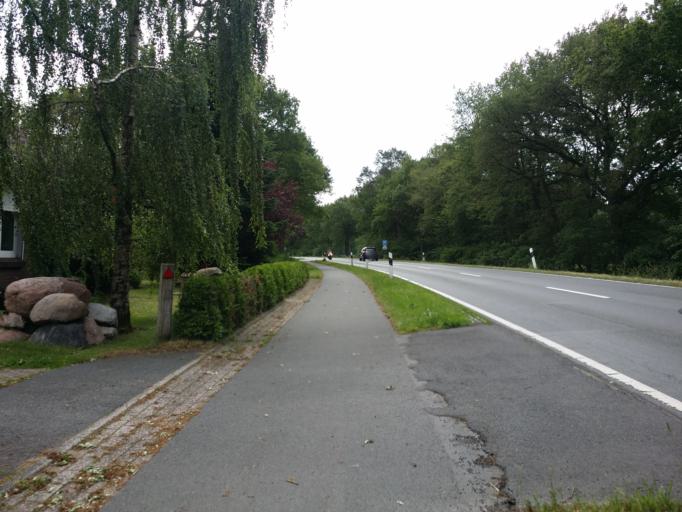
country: DE
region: Lower Saxony
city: Wittmund
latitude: 53.5129
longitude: 7.7955
